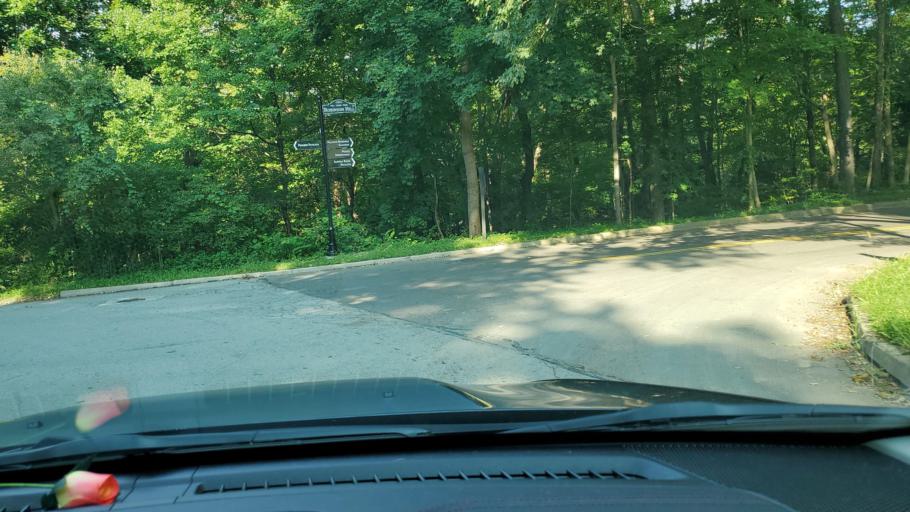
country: US
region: Ohio
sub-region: Mahoning County
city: Youngstown
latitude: 41.0850
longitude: -80.6792
